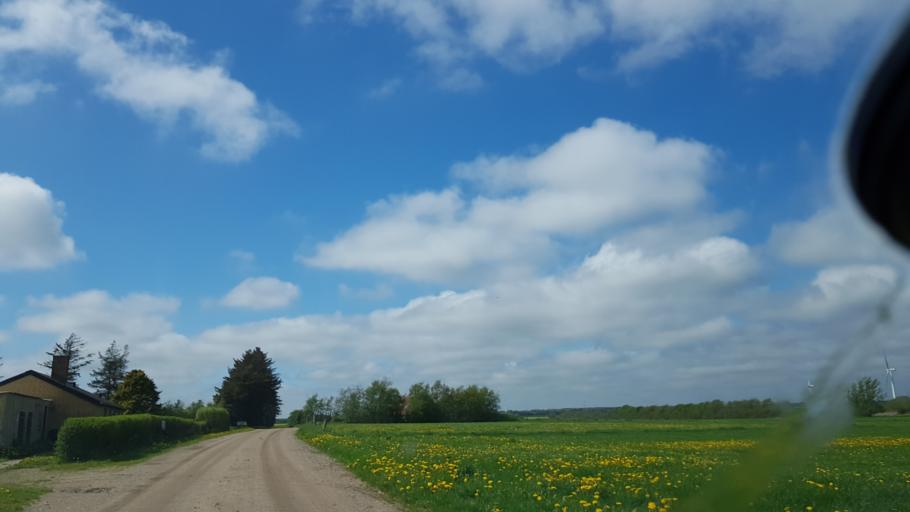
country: DK
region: South Denmark
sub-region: Tonder Kommune
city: Sherrebek
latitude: 55.1300
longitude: 8.8151
